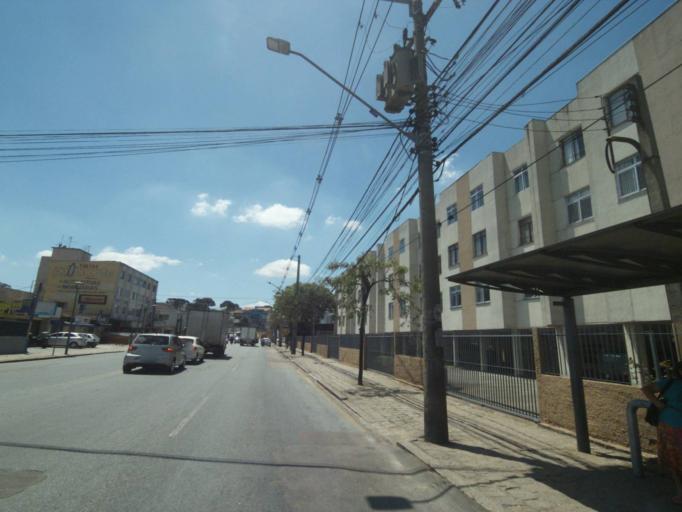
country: BR
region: Parana
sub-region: Curitiba
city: Curitiba
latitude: -25.3915
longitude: -49.2248
